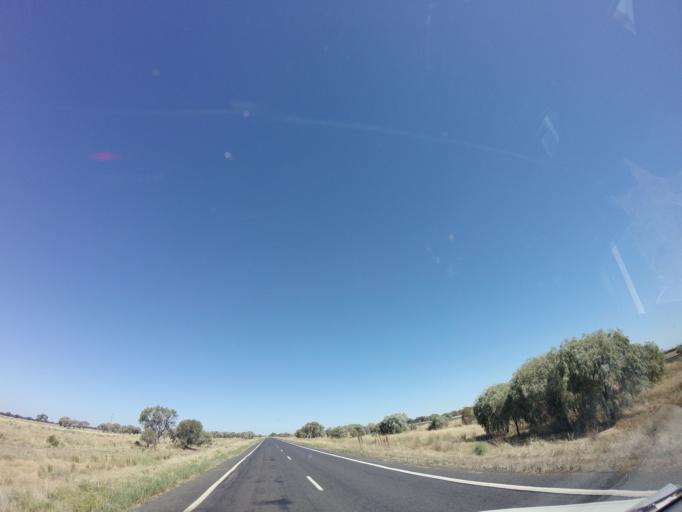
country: AU
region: New South Wales
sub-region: Bogan
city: Nyngan
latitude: -31.6140
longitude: 147.2945
